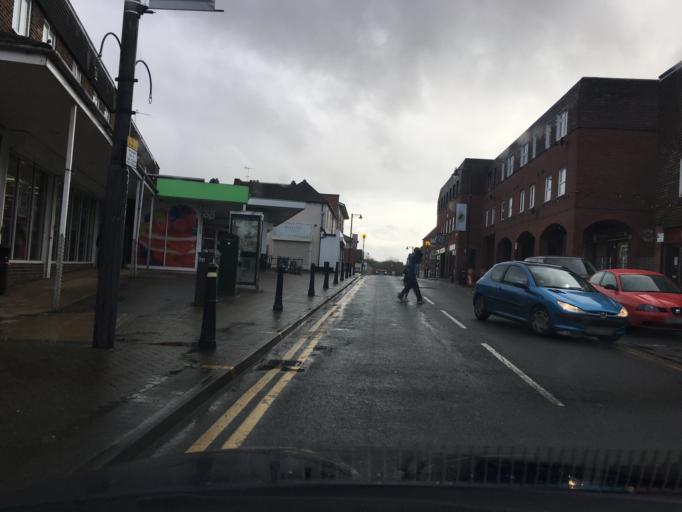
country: GB
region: England
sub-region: Bracknell Forest
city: Crowthorne
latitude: 51.3688
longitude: -0.7931
